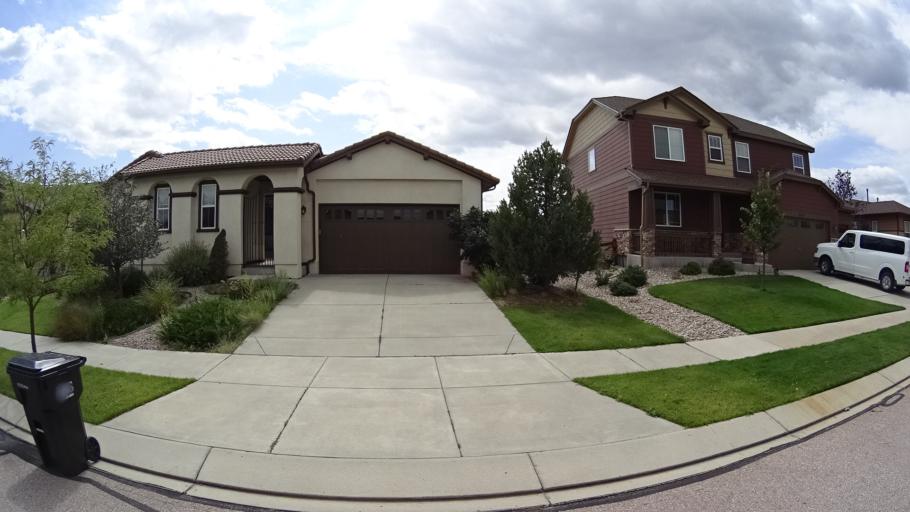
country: US
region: Colorado
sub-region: El Paso County
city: Cimarron Hills
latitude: 38.9360
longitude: -104.6774
